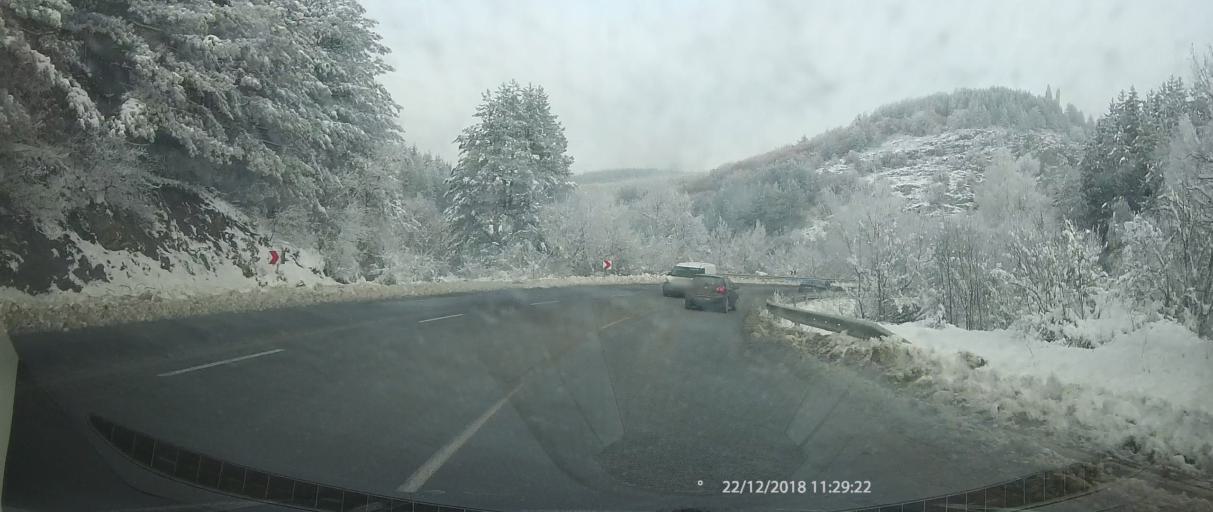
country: BG
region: Kyustendil
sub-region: Obshtina Bobovdol
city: Bobovdol
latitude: 42.2690
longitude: 22.9589
